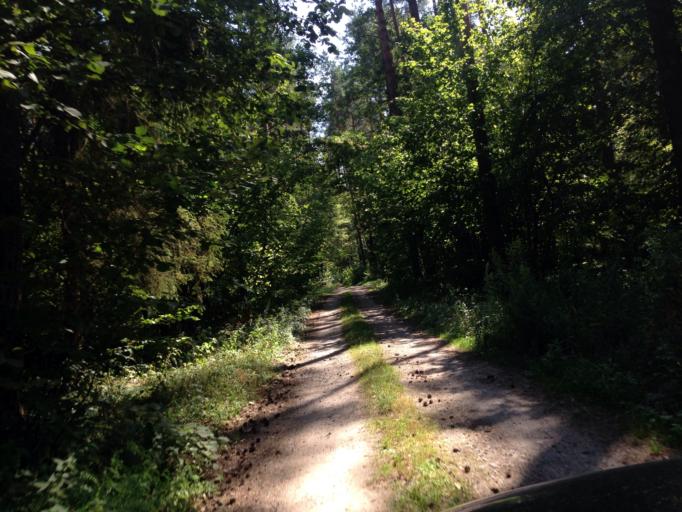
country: PL
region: Kujawsko-Pomorskie
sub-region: Powiat brodnicki
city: Bartniczka
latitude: 53.2719
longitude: 19.5697
